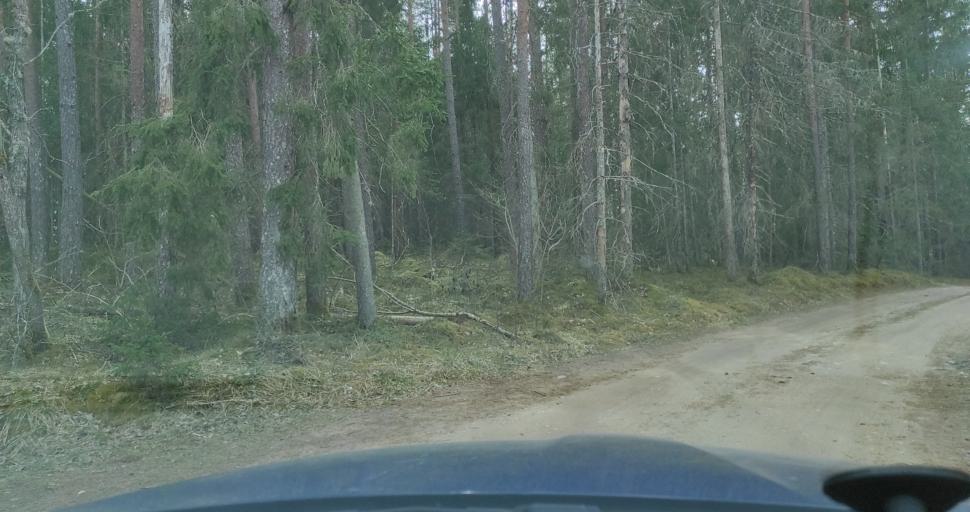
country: LV
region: Talsu Rajons
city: Stende
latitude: 57.0887
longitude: 22.3995
